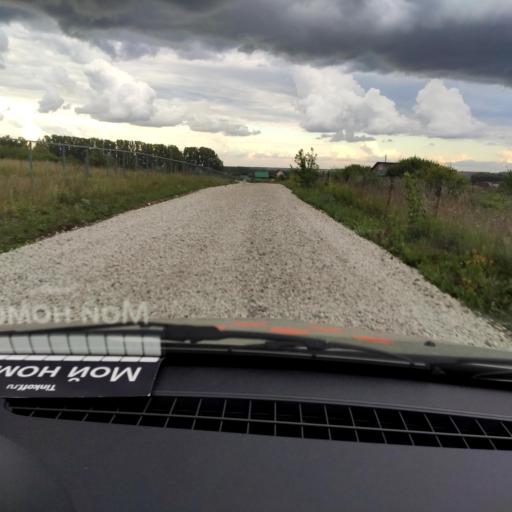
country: RU
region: Bashkortostan
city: Avdon
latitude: 54.5159
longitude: 55.8355
